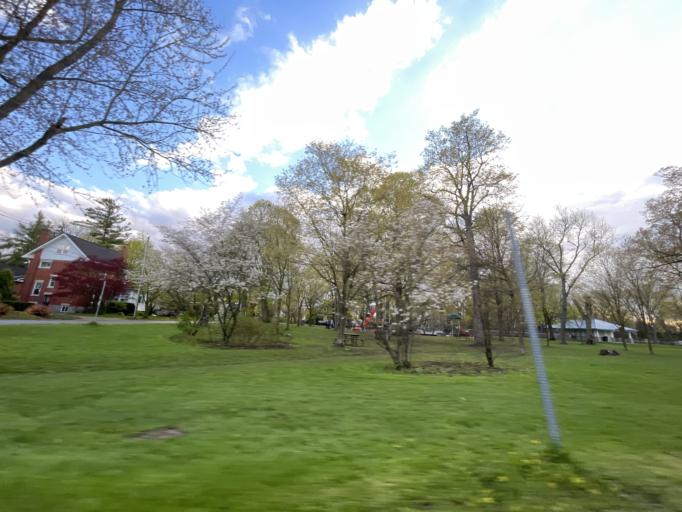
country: CA
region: Ontario
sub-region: Wellington County
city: Guelph
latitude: 43.5518
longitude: -80.2421
